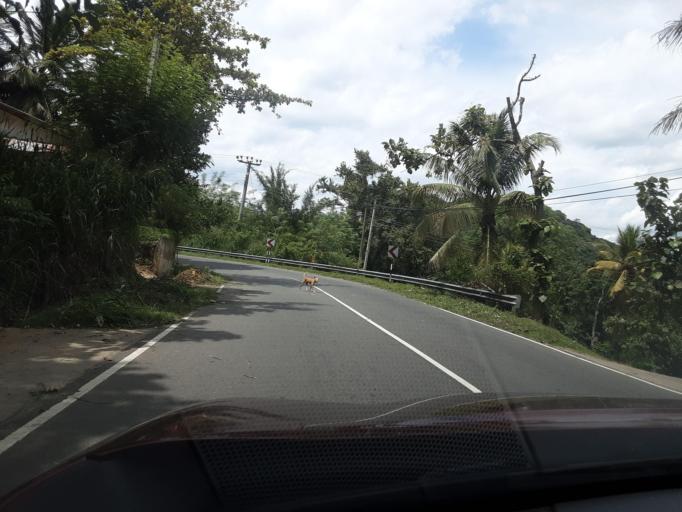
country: LK
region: Uva
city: Monaragala
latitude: 6.8966
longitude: 81.2729
